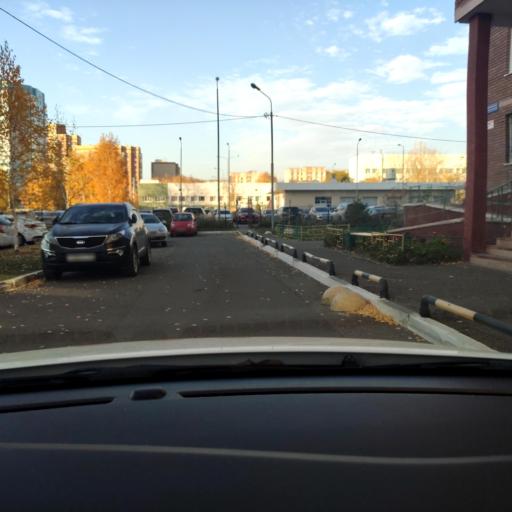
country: RU
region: Tatarstan
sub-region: Gorod Kazan'
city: Kazan
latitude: 55.8334
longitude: 49.1362
